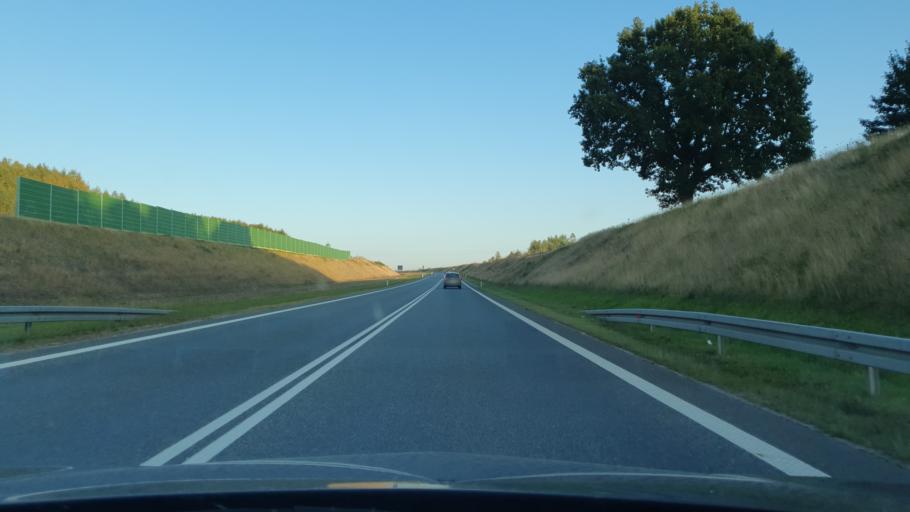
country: PL
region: Pomeranian Voivodeship
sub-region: Powiat slupski
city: Kobylnica
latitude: 54.4298
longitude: 16.9768
